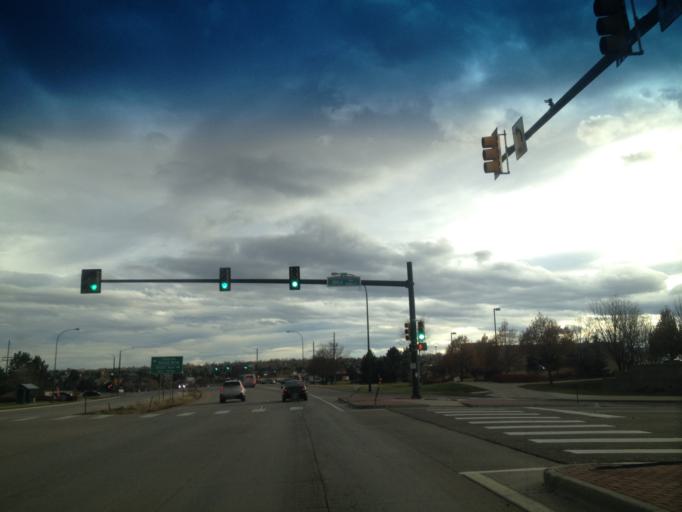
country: US
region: Colorado
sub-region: Broomfield County
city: Broomfield
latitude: 39.8799
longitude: -105.0963
